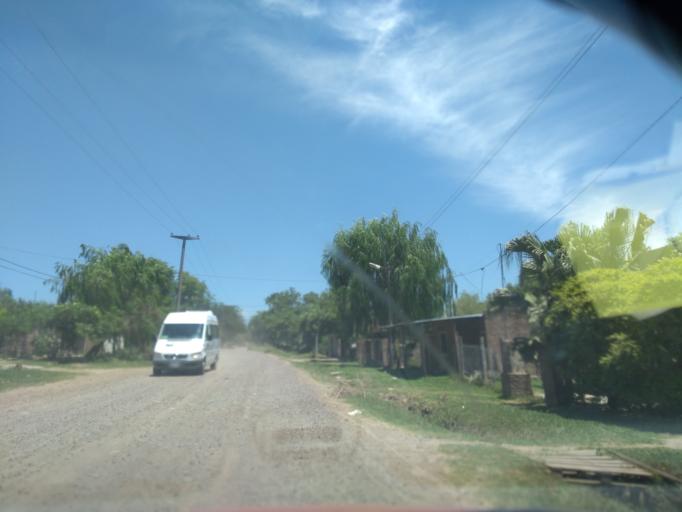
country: AR
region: Chaco
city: Resistencia
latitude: -27.4674
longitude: -58.9616
